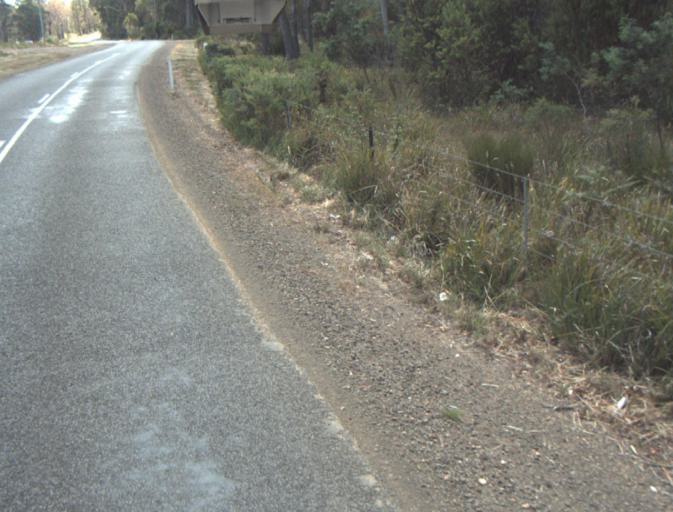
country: AU
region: Tasmania
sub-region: Launceston
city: Mayfield
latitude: -41.3244
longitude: 147.1374
